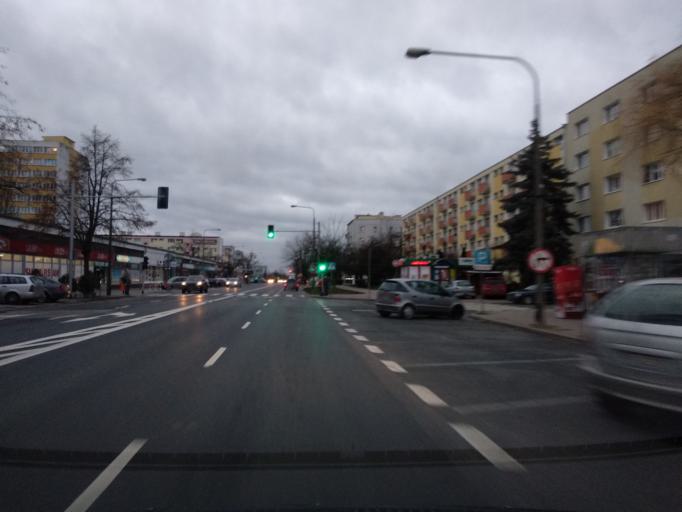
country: PL
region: Greater Poland Voivodeship
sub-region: Konin
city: Konin
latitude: 52.2289
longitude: 18.2496
